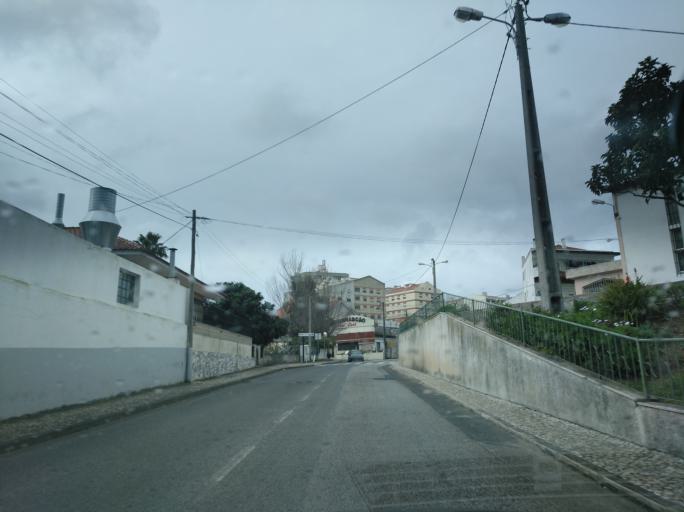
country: PT
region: Lisbon
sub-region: Odivelas
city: Famoes
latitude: 38.7904
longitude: -9.2080
